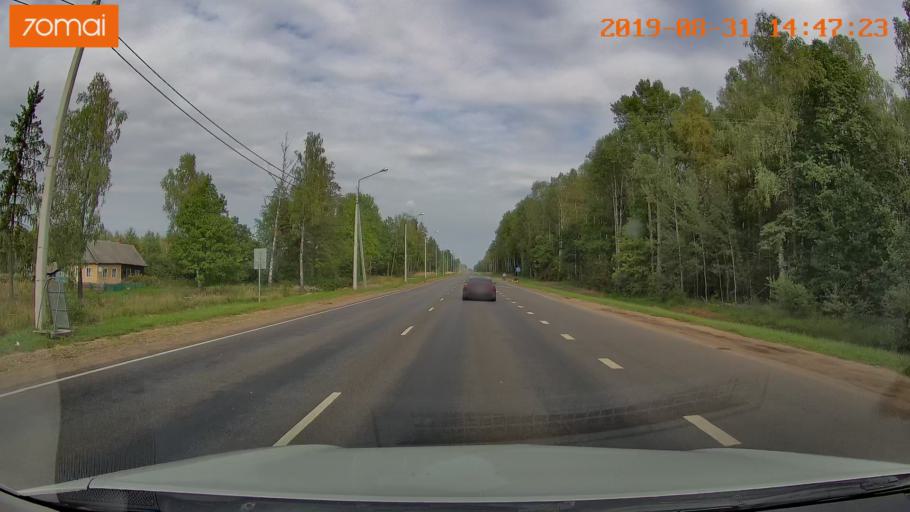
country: RU
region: Kaluga
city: Betlitsa
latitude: 54.2391
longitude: 33.7248
